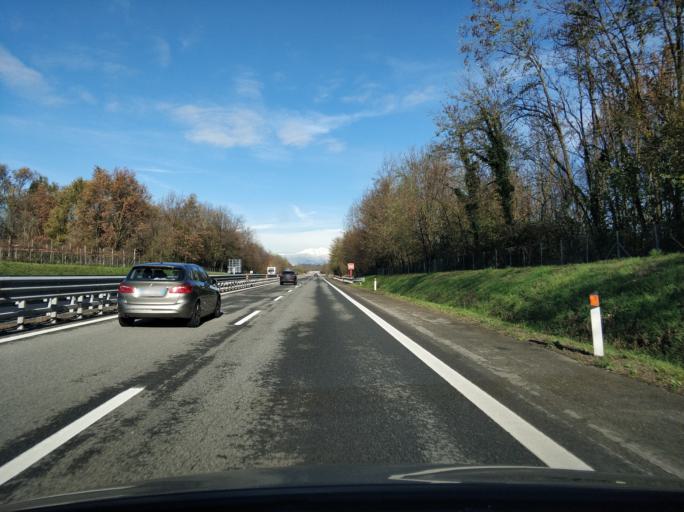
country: IT
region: Piedmont
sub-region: Provincia di Torino
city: San Giusto Canavese
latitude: 45.3220
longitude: 7.8222
